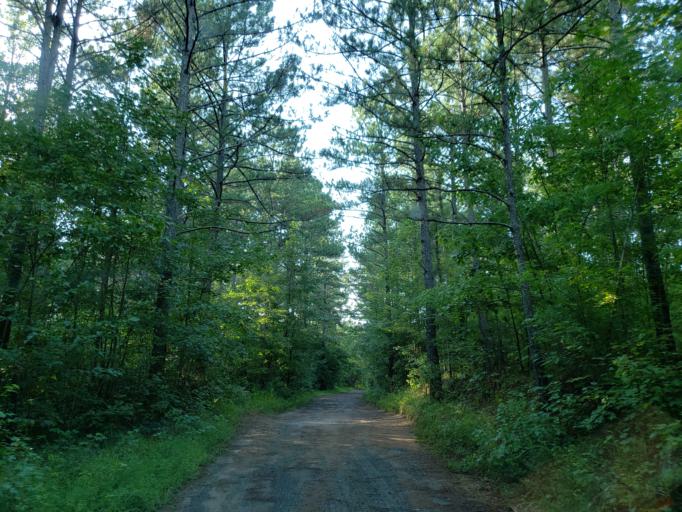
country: US
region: Georgia
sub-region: Bartow County
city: Emerson
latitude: 34.1875
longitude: -84.6476
